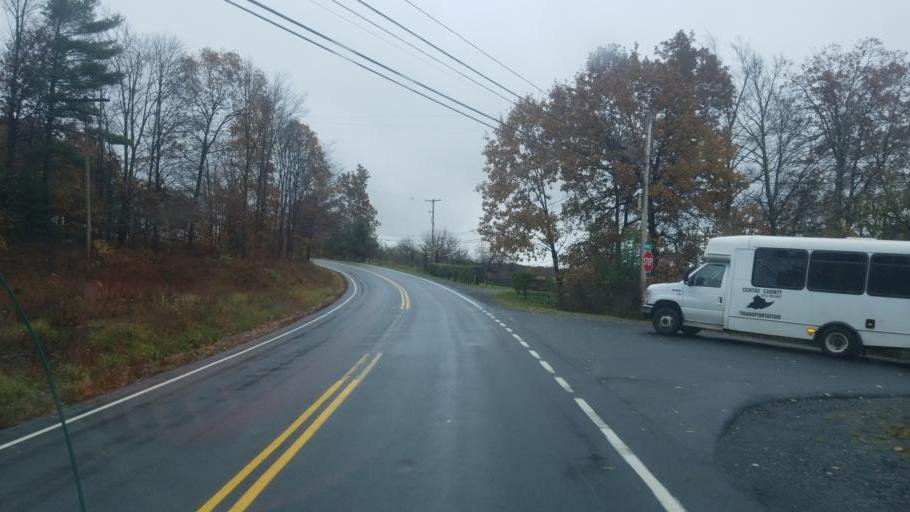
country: US
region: Pennsylvania
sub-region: Centre County
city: Milesburg
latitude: 41.0306
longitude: -77.9843
